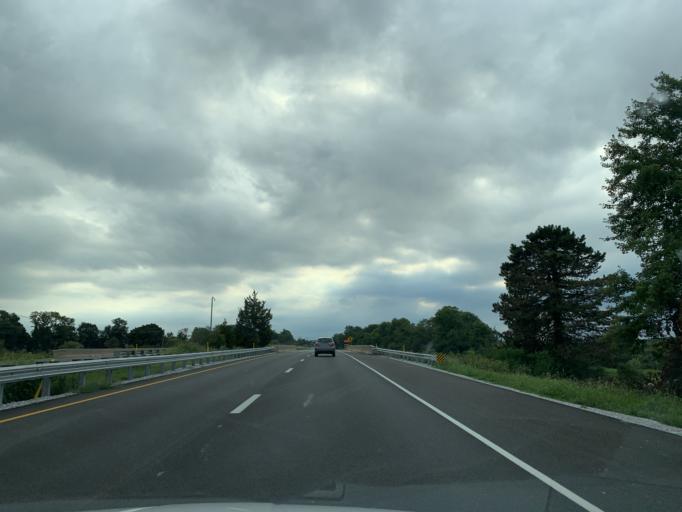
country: US
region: Pennsylvania
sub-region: York County
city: Shiloh
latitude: 39.9377
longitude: -76.7976
